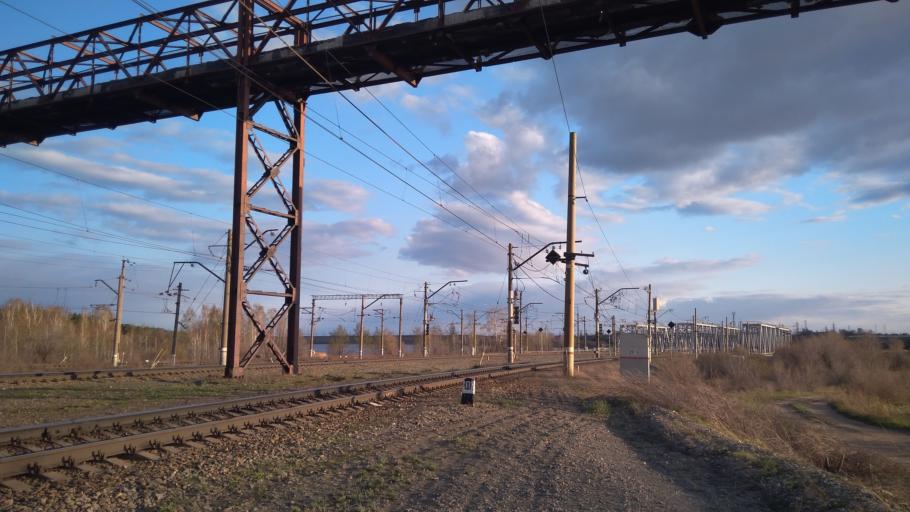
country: RU
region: Chelyabinsk
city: Troitsk
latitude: 54.0584
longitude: 61.6134
